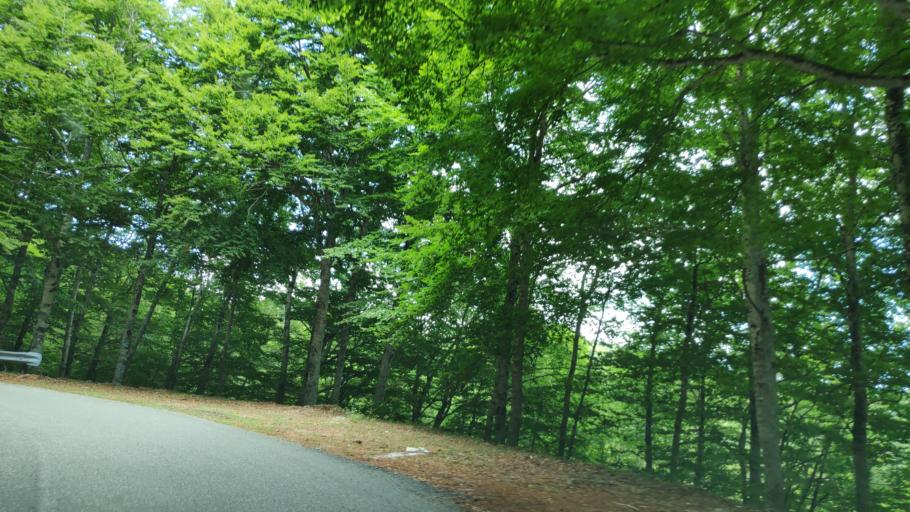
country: IT
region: Calabria
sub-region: Provincia di Vibo-Valentia
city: Nardodipace
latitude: 38.5011
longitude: 16.3533
